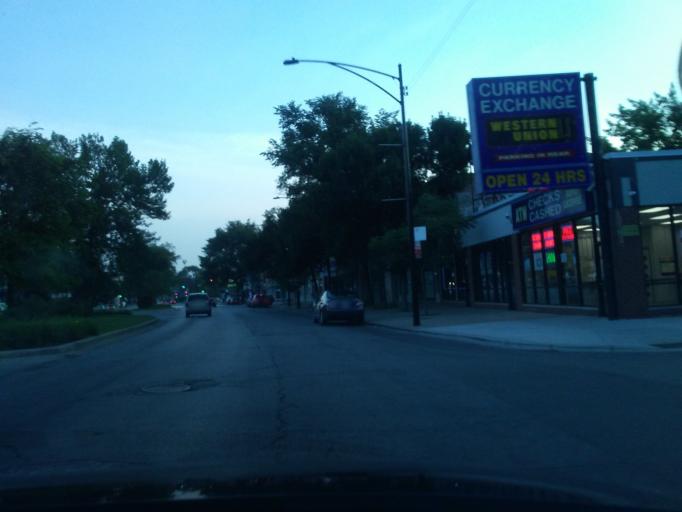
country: US
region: Illinois
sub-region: Cook County
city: Evanston
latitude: 41.9964
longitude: -87.6701
